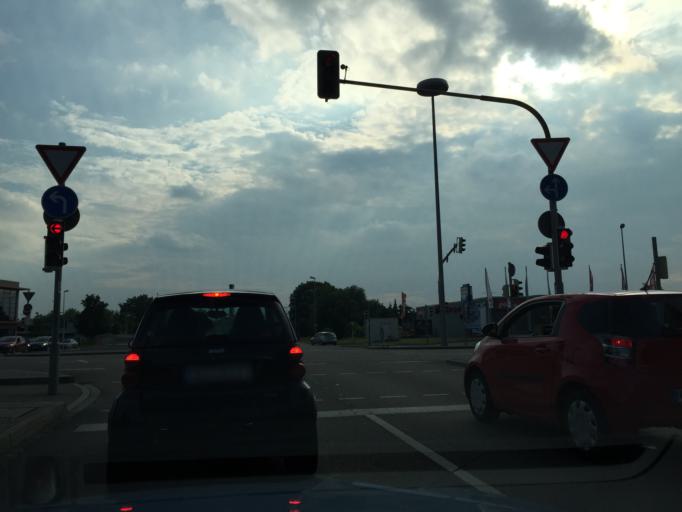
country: DE
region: Bavaria
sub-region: Swabia
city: Neu-Ulm
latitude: 48.3831
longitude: 10.0057
